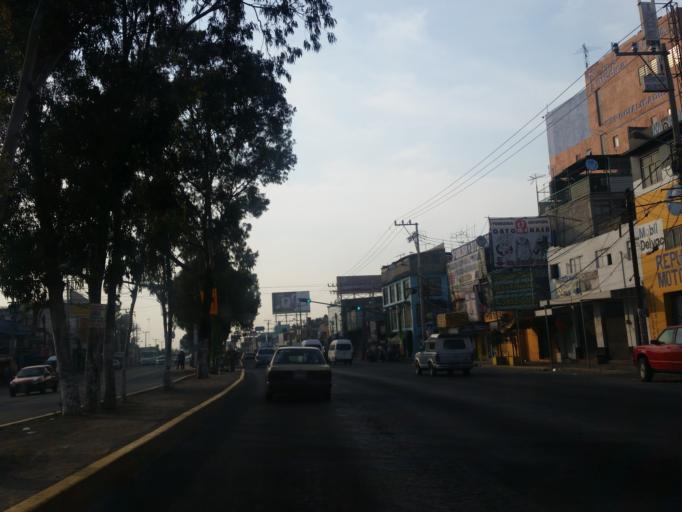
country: MX
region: Mexico
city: Los Reyes La Paz
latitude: 19.3555
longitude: -98.9795
